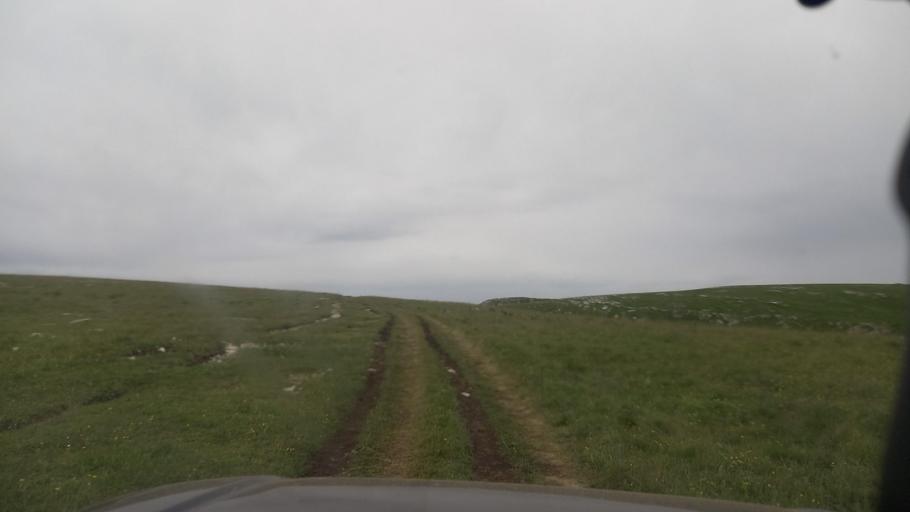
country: RU
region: Karachayevo-Cherkesiya
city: Pregradnaya
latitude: 43.9756
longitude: 41.2911
